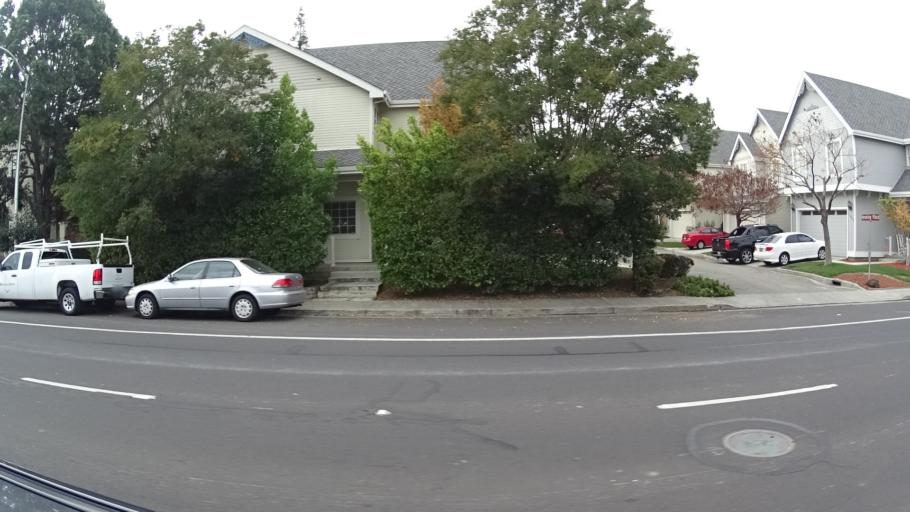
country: US
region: California
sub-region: Santa Clara County
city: Santa Clara
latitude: 37.3410
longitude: -121.9510
